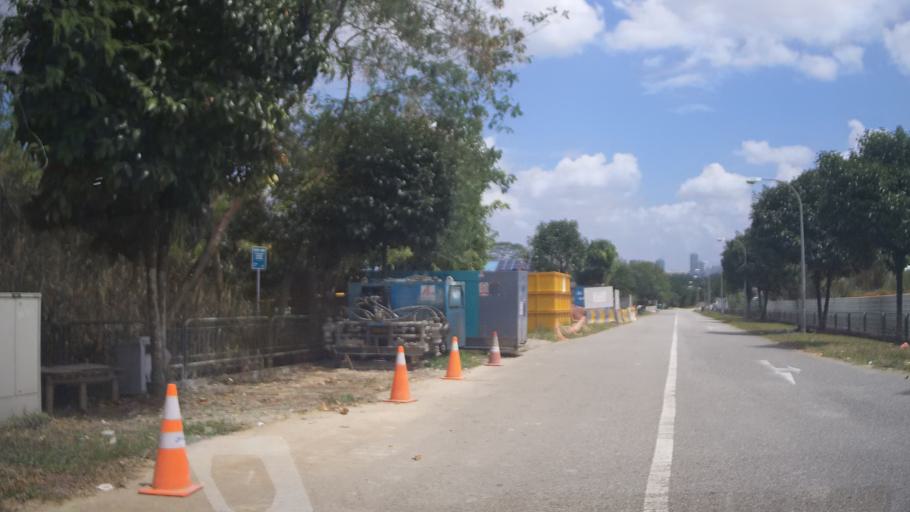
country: MY
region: Johor
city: Johor Bahru
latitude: 1.4381
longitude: 103.7262
